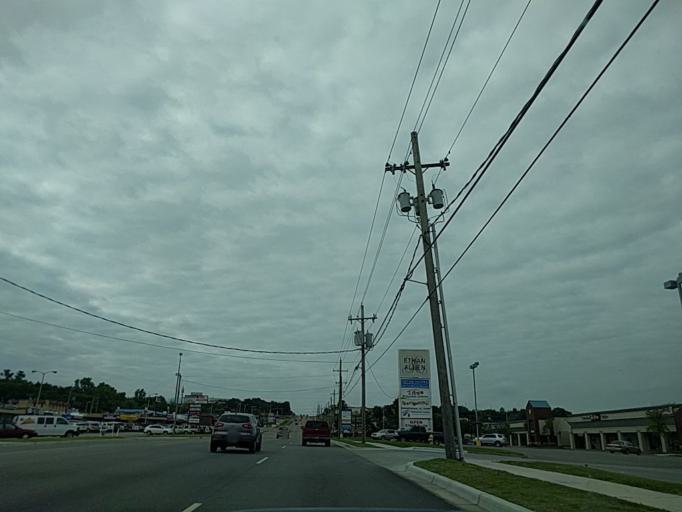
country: US
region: Oklahoma
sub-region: Tulsa County
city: Jenks
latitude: 36.0779
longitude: -95.9044
